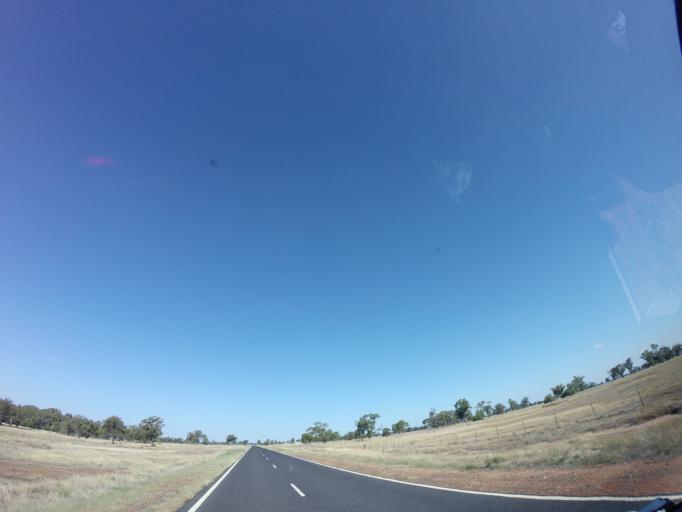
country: AU
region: New South Wales
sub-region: Gilgandra
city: Gilgandra
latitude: -31.6618
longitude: 148.3542
